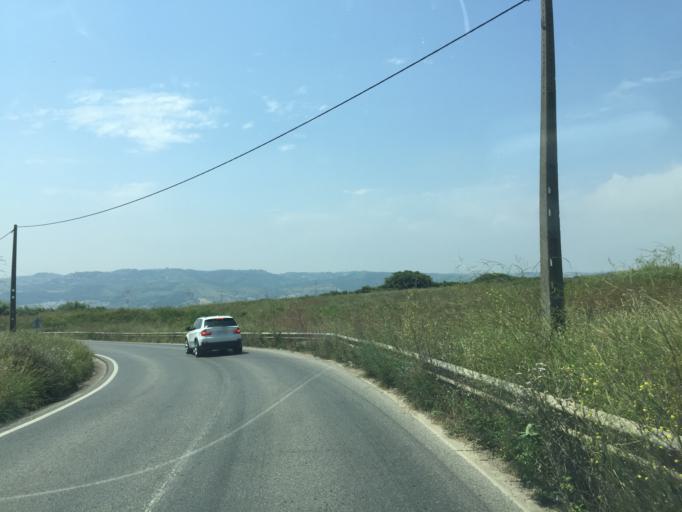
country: PT
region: Lisbon
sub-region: Loures
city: Loures
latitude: 38.8771
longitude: -9.1850
